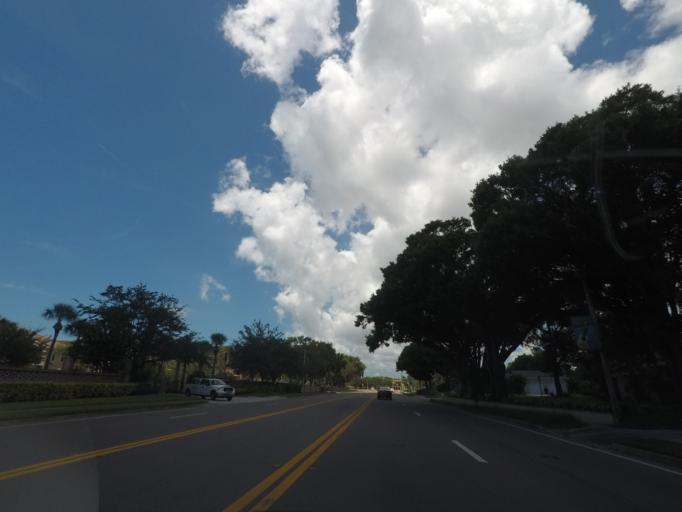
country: US
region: Florida
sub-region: Pinellas County
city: Gulfport
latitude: 27.7522
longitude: -82.7175
